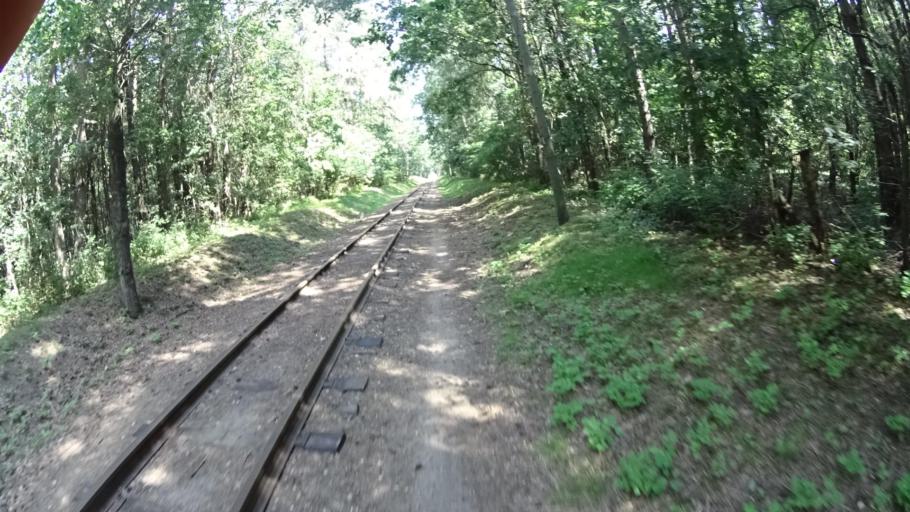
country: PL
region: Masovian Voivodeship
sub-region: Powiat piaseczynski
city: Tarczyn
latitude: 51.9949
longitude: 20.8958
